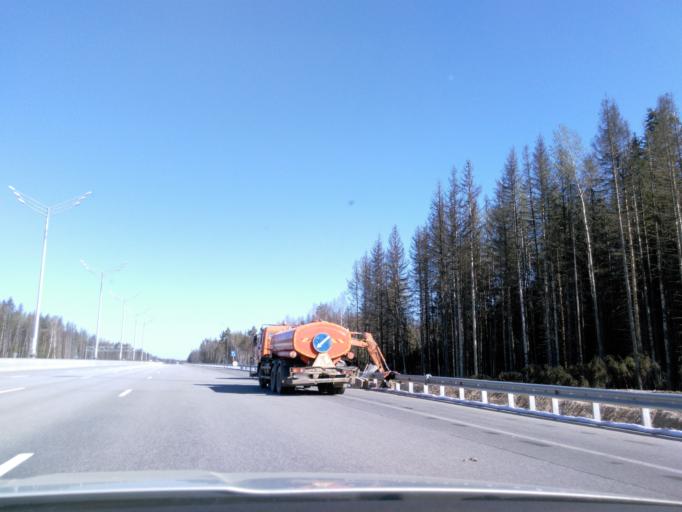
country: RU
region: Moskovskaya
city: Rzhavki
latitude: 56.0080
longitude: 37.2887
